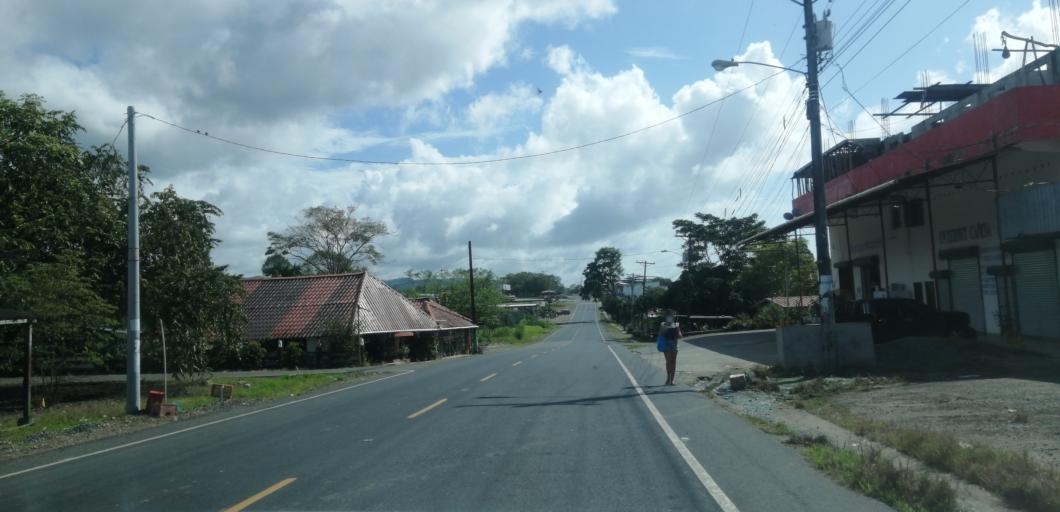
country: PA
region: Panama
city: Canita
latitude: 9.2214
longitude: -78.8961
